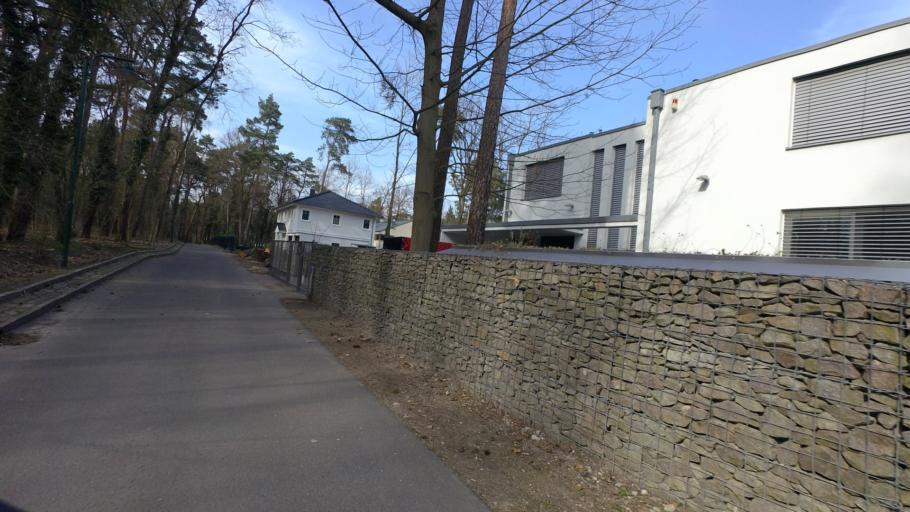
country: DE
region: Brandenburg
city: Kleinmachnow
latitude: 52.4106
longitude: 13.2024
